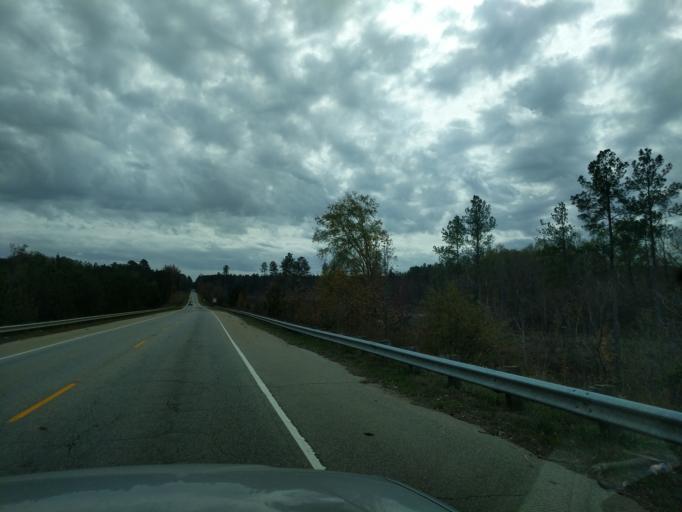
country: US
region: South Carolina
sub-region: Greenwood County
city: Ninety Six
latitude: 34.1747
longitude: -81.8644
